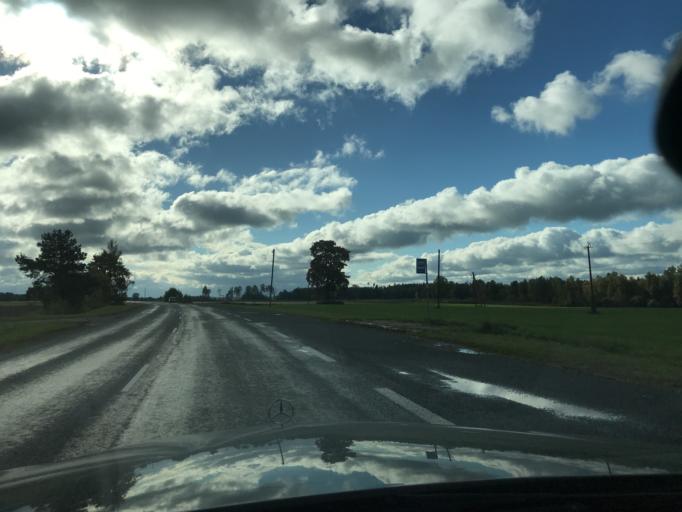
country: EE
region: Valgamaa
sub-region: Valga linn
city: Valga
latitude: 57.9736
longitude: 26.2602
